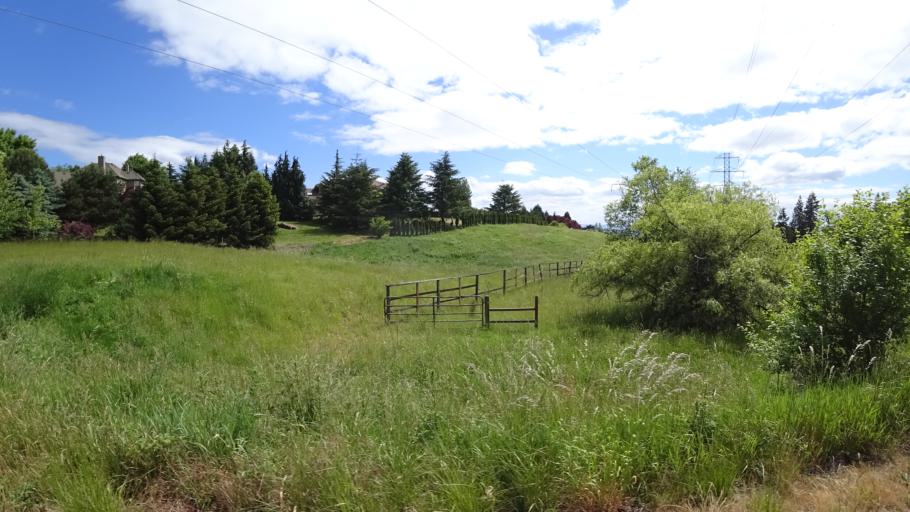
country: US
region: Oregon
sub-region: Washington County
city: Oak Hills
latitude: 45.5963
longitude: -122.8244
